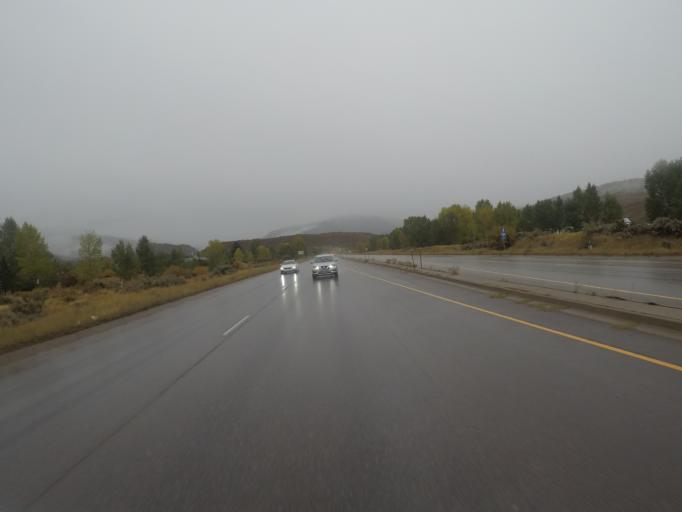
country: US
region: Colorado
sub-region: Pitkin County
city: Aspen
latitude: 39.2231
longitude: -106.8651
